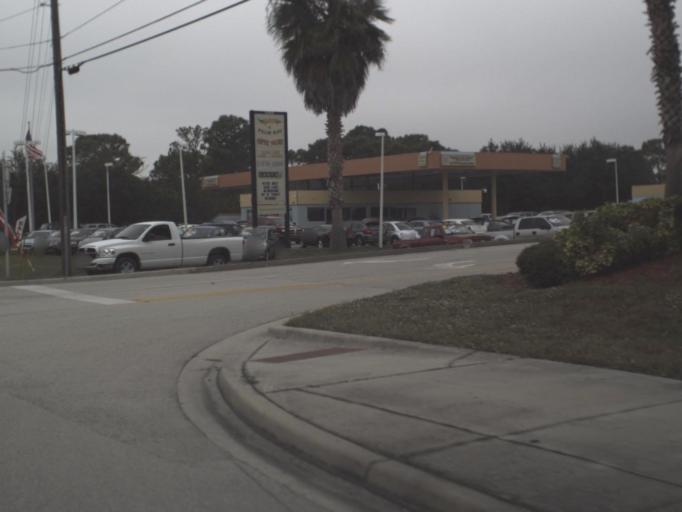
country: US
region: Florida
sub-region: Brevard County
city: West Melbourne
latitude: 28.0354
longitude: -80.6420
